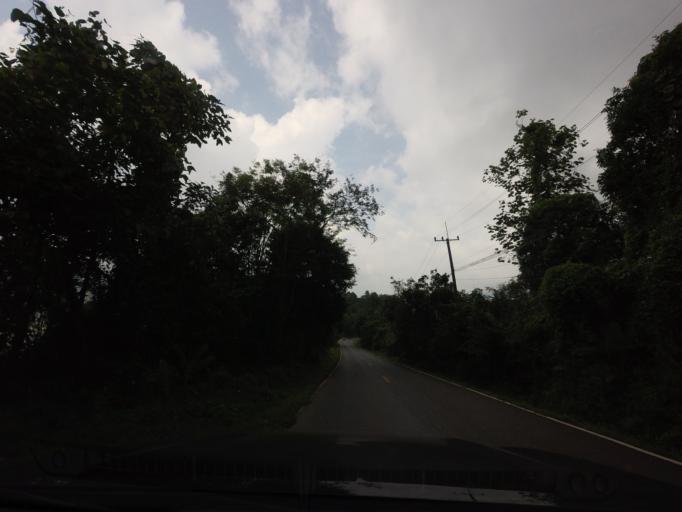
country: TH
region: Nan
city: Bo Kluea
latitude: 19.1938
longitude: 101.0466
